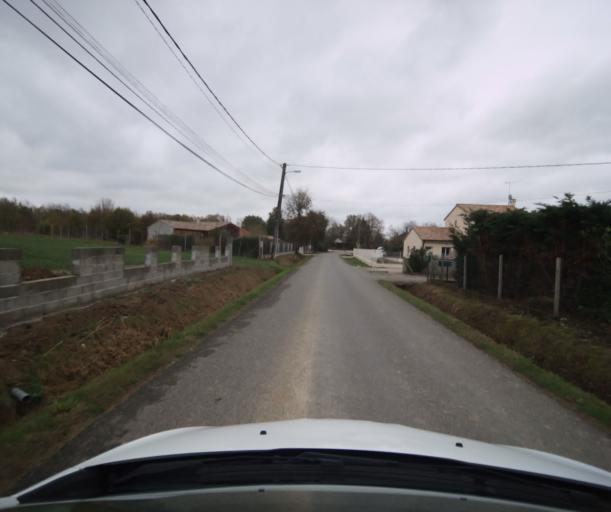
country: FR
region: Midi-Pyrenees
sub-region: Departement du Tarn-et-Garonne
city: Saint-Porquier
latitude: 44.0424
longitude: 1.1552
